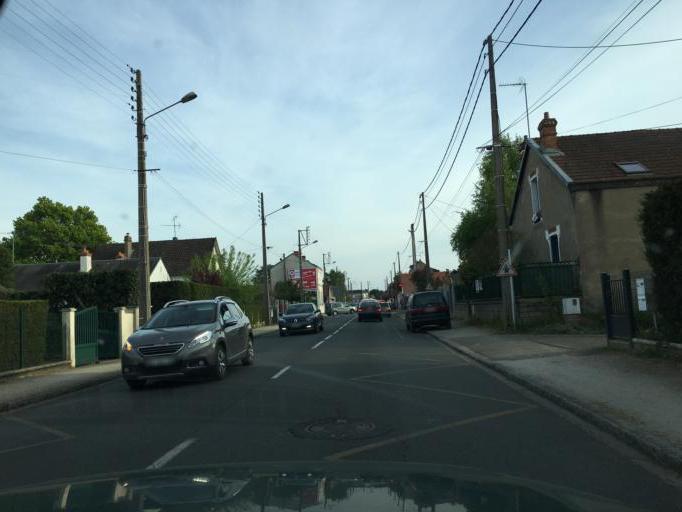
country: FR
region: Centre
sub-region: Departement du Loiret
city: Fleury-les-Aubrais
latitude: 47.9222
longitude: 1.9143
